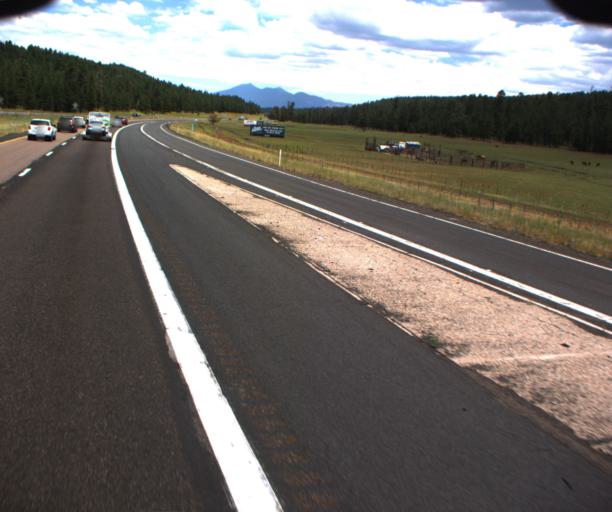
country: US
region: Arizona
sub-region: Coconino County
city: Mountainaire
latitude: 35.0209
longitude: -111.6852
